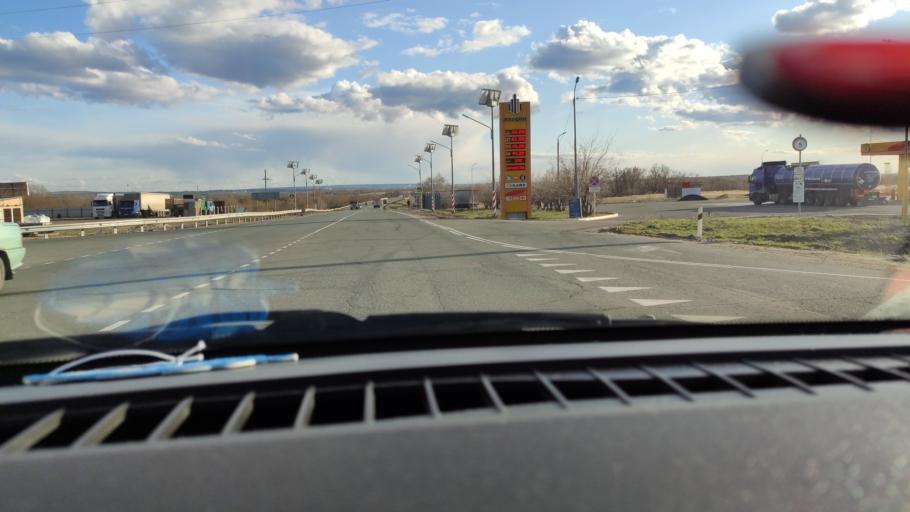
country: RU
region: Saratov
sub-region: Saratovskiy Rayon
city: Saratov
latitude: 51.7274
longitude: 46.0306
